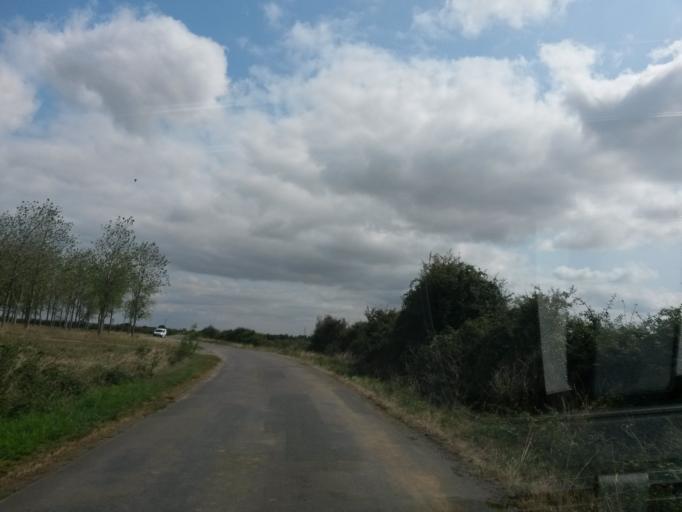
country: FR
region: Pays de la Loire
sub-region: Departement de la Vendee
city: Saint-Hilaire-de-Talmont
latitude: 46.4410
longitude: -1.6041
